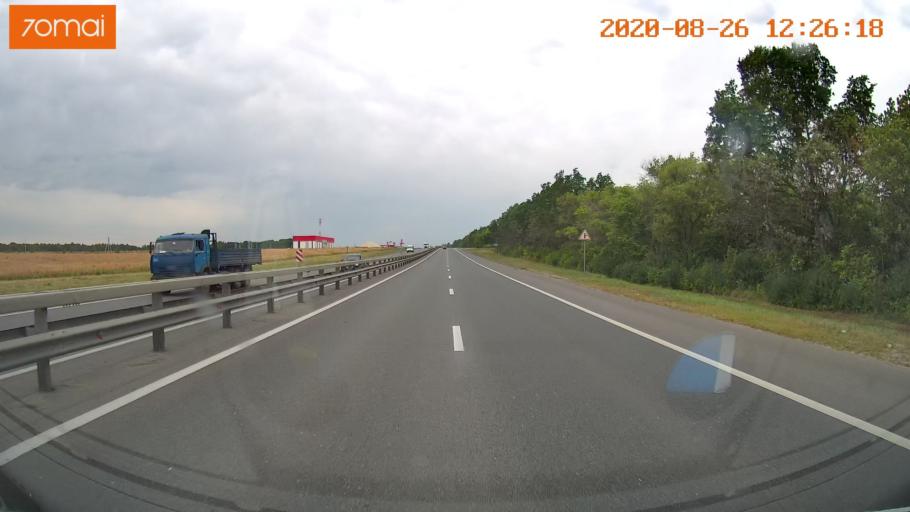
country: RU
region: Rjazan
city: Polyany
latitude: 54.5335
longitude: 39.8627
